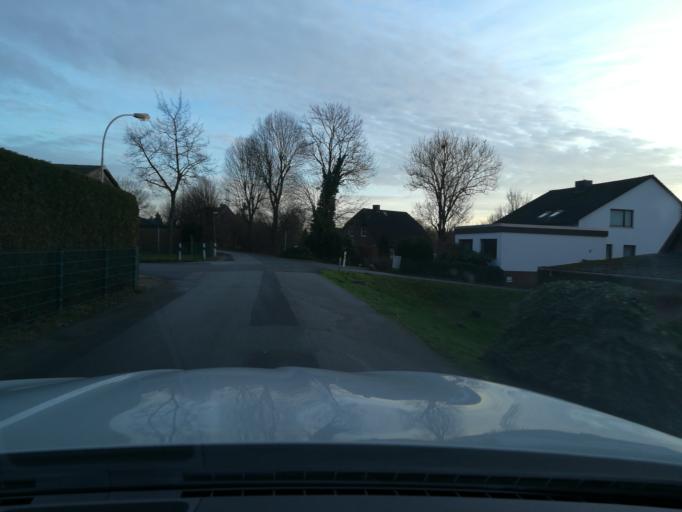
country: DE
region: Lower Saxony
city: Stelle
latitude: 53.4476
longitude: 10.0737
